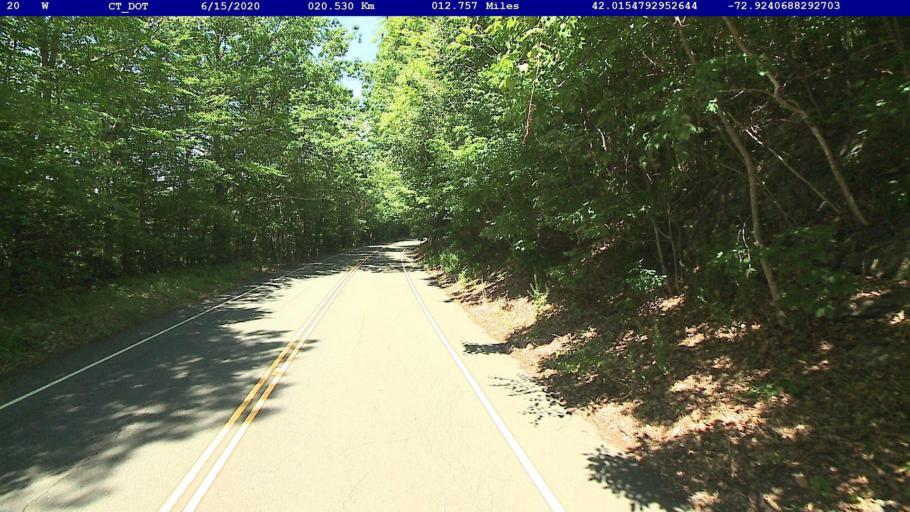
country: US
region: Massachusetts
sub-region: Hampden County
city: Granville
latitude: 42.0146
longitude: -72.9245
